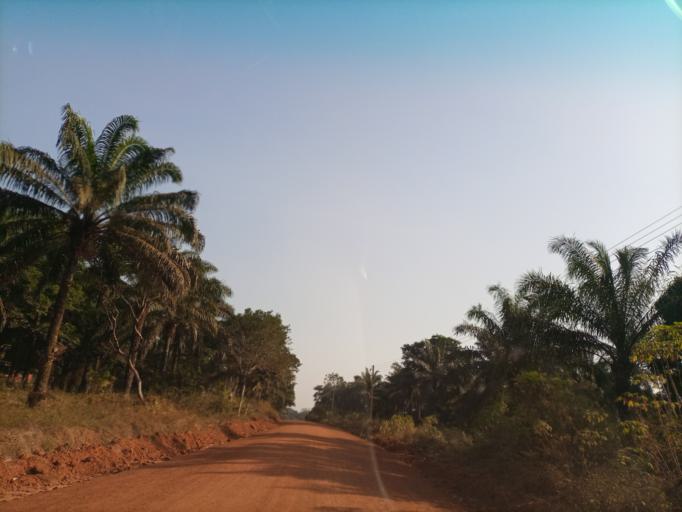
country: NG
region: Enugu
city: Opi
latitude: 6.7714
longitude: 7.3914
